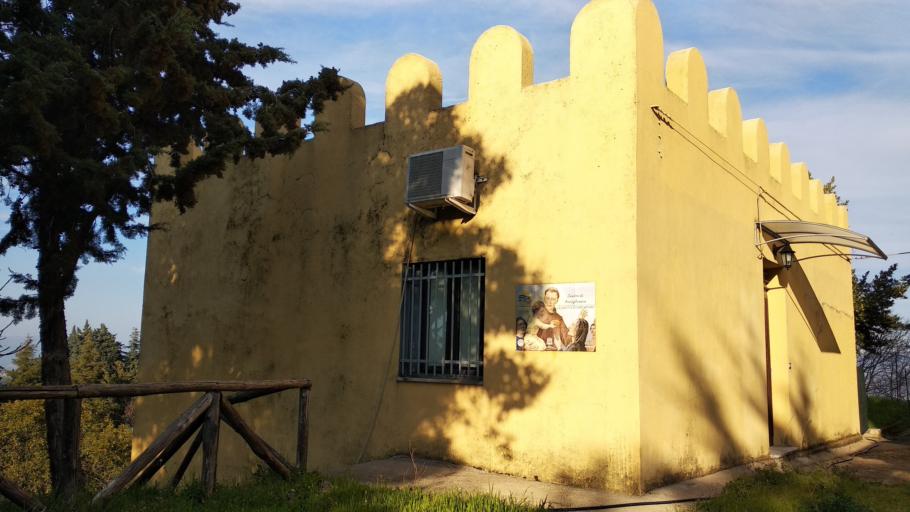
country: IT
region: Calabria
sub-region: Provincia di Cosenza
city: San Marco Argentano
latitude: 39.5568
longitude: 16.1235
